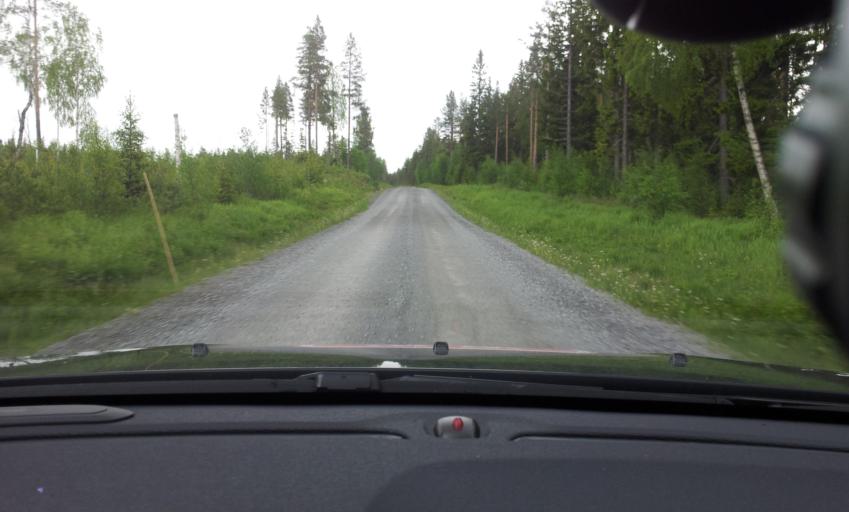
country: SE
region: Jaemtland
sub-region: OEstersunds Kommun
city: Brunflo
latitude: 63.1384
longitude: 15.0658
